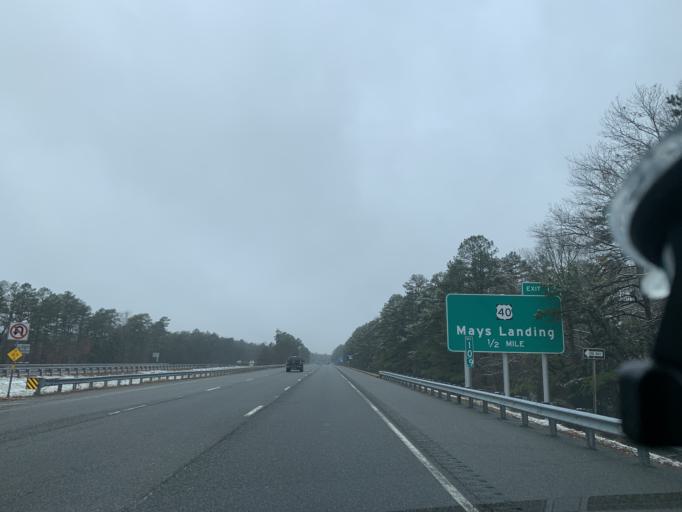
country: US
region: New Jersey
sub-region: Atlantic County
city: Pomona
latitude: 39.4428
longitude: -74.6096
